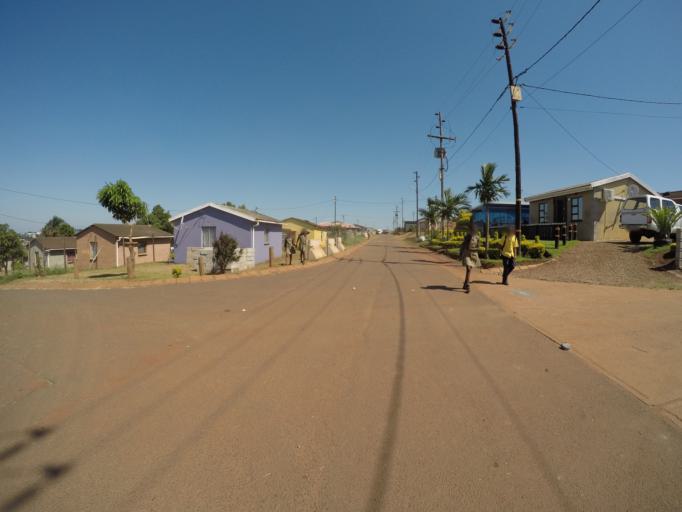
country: ZA
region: KwaZulu-Natal
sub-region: uThungulu District Municipality
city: Empangeni
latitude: -28.7698
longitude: 31.8781
